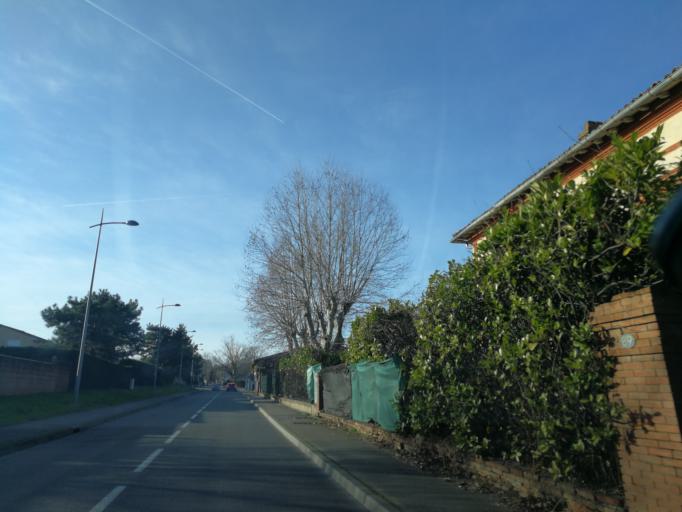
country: FR
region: Midi-Pyrenees
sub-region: Departement de la Haute-Garonne
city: Saint-Jean
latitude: 43.6505
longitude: 1.5014
